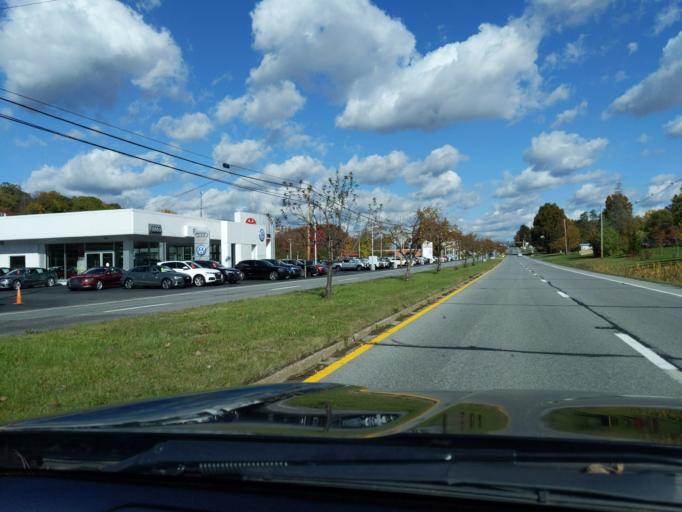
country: US
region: Pennsylvania
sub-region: Blair County
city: Lakemont
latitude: 40.4504
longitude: -78.3939
